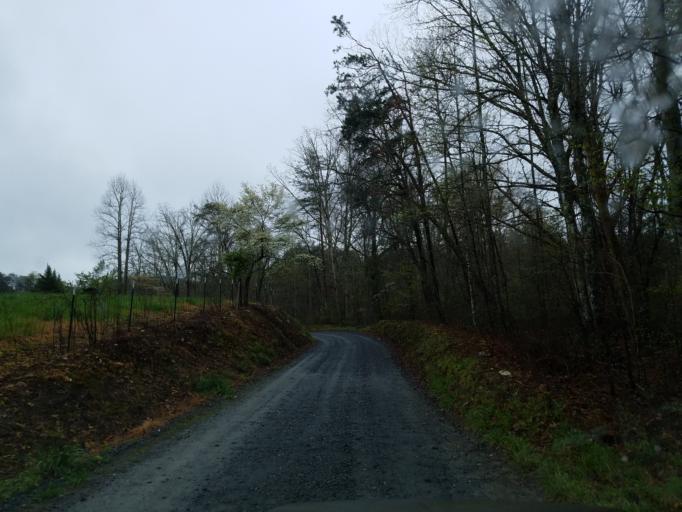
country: US
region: Georgia
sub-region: Fannin County
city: Blue Ridge
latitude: 34.8569
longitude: -84.2332
